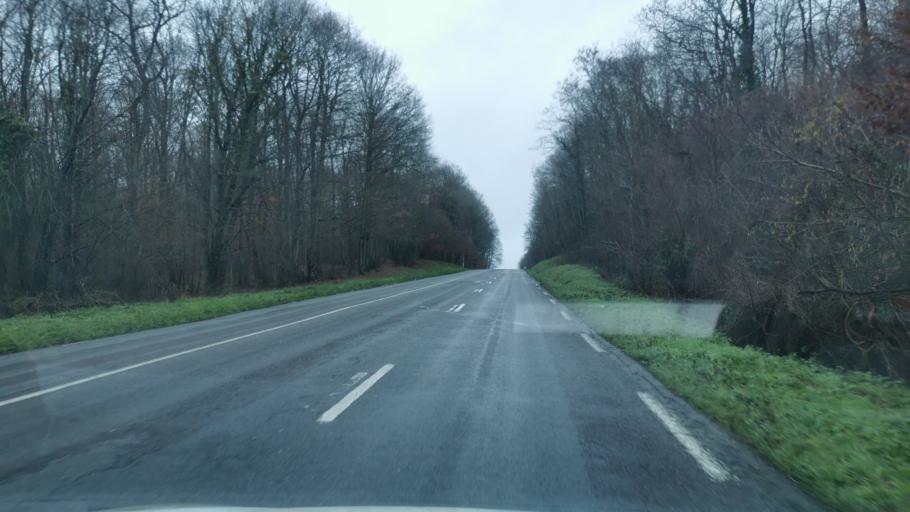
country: FR
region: Haute-Normandie
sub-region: Departement de l'Eure
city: Normanville
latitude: 49.0750
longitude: 1.1771
